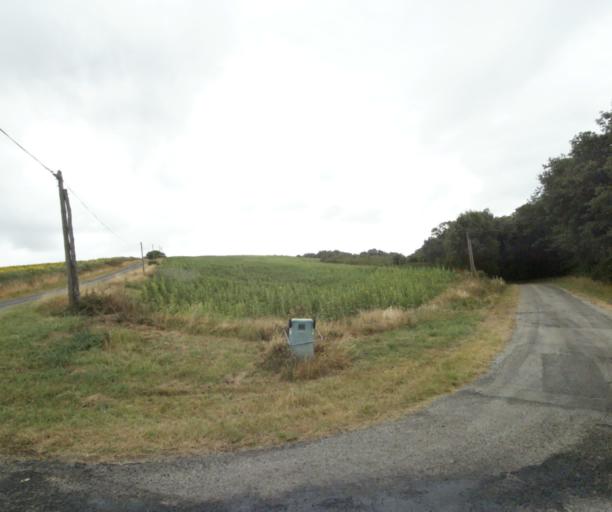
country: FR
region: Midi-Pyrenees
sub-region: Departement de la Haute-Garonne
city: Revel
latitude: 43.3894
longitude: 2.0297
